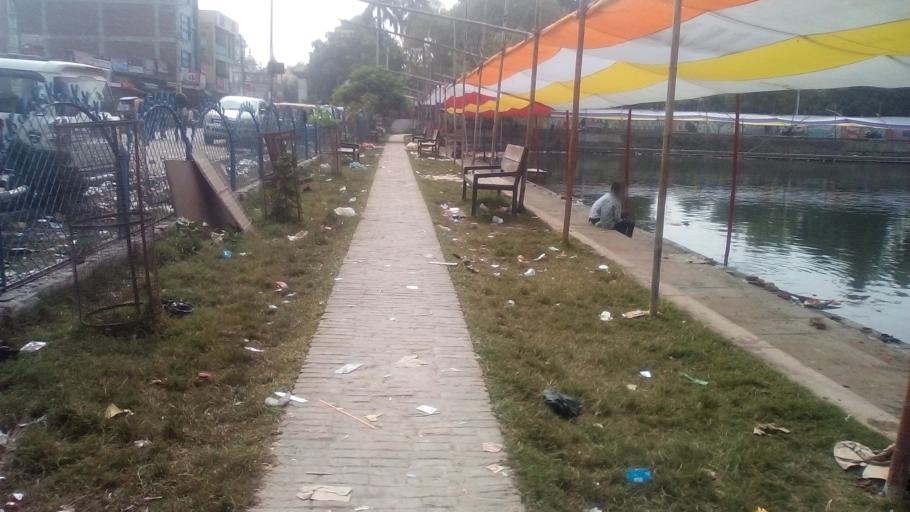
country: NP
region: Central Region
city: Janakpur
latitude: 26.7319
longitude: 85.9259
